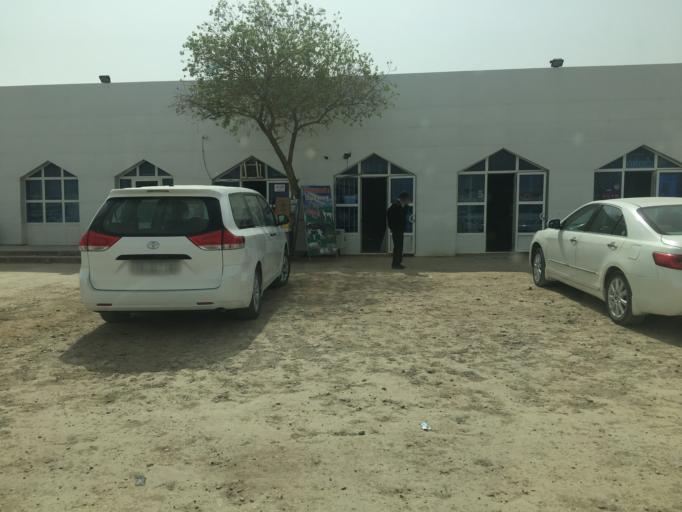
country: TM
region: Ahal
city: Tejen
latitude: 37.3690
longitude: 60.4989
